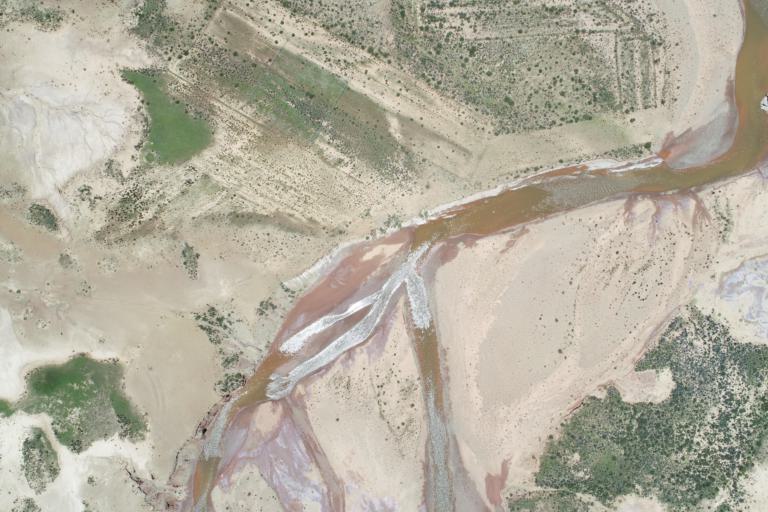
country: BO
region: La Paz
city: Curahuara de Carangas
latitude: -17.3056
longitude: -68.4953
